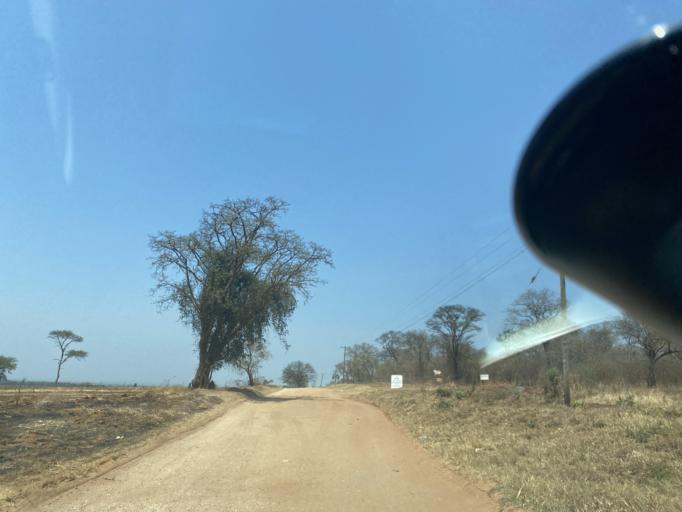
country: ZM
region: Lusaka
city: Kafue
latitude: -15.5455
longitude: 28.0708
